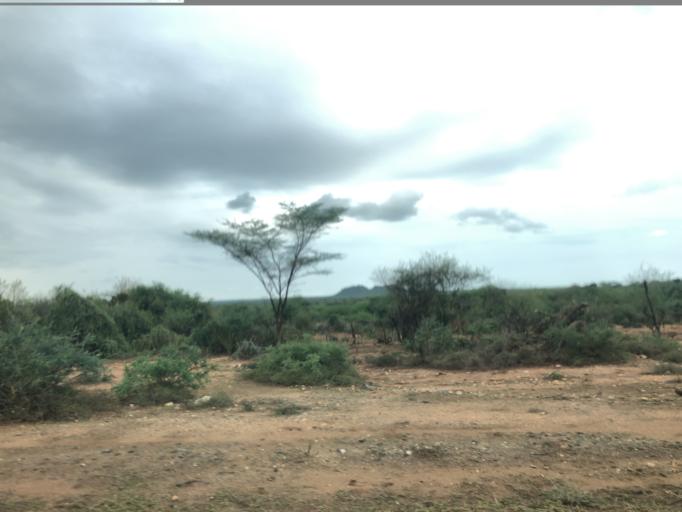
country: ET
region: Southern Nations, Nationalities, and People's Region
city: Turmi
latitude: 5.0757
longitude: 36.5069
